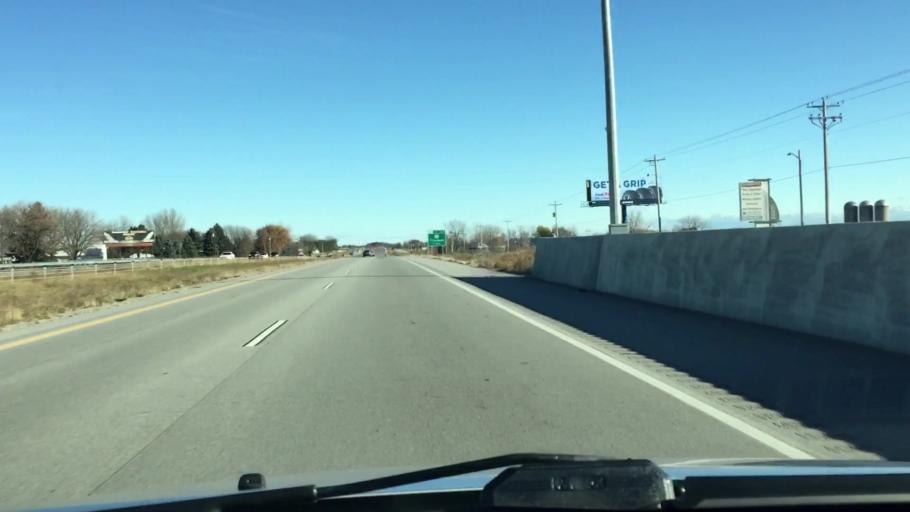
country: US
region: Wisconsin
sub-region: Brown County
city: Wrightstown
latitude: 44.3680
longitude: -88.1765
